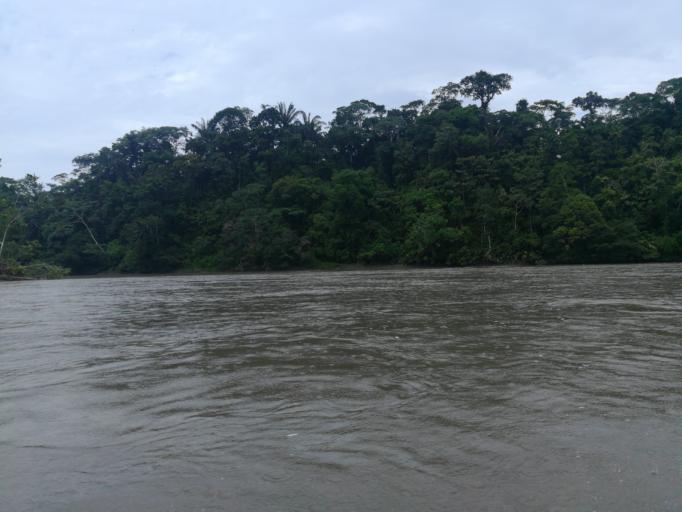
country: EC
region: Orellana
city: Boca Suno
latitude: -0.7628
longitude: -77.1711
